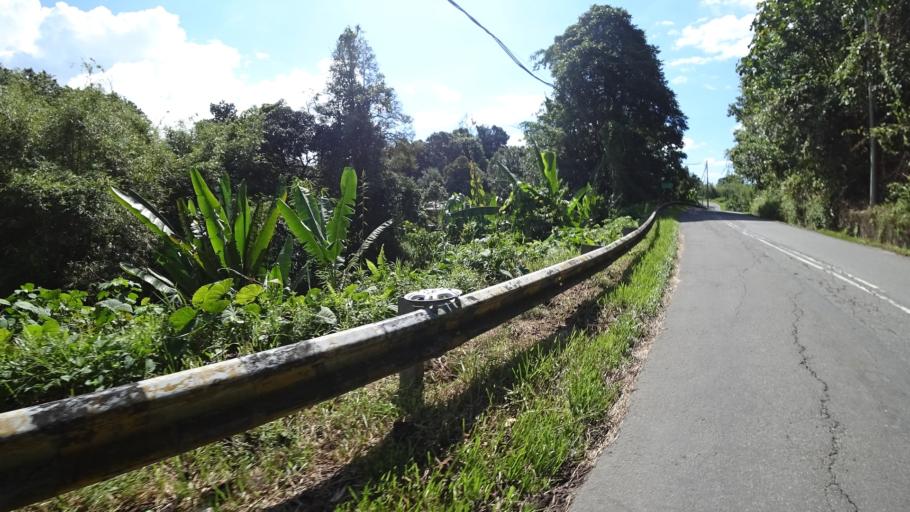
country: BN
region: Tutong
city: Tutong
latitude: 4.7544
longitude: 114.7891
